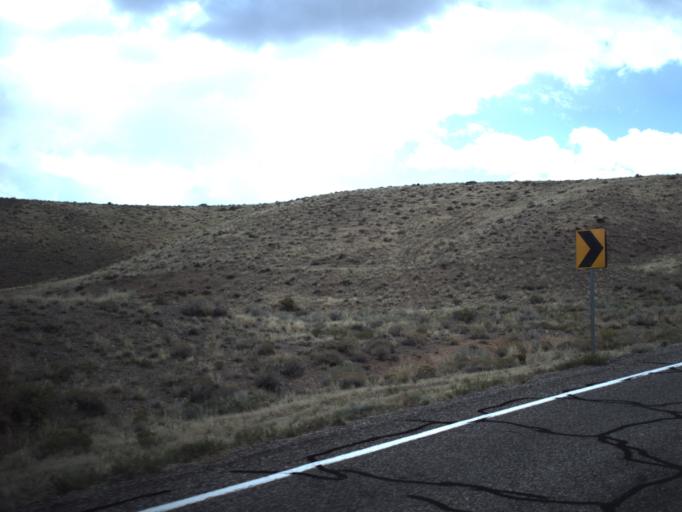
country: US
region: Utah
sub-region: Sevier County
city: Monroe
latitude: 38.6331
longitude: -112.1878
